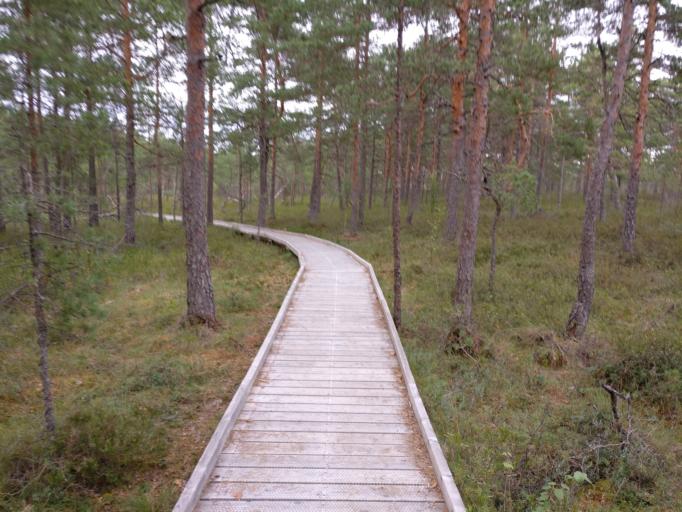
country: EE
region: Paernumaa
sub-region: Vaendra vald (alev)
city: Vandra
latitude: 58.4918
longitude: 24.9840
